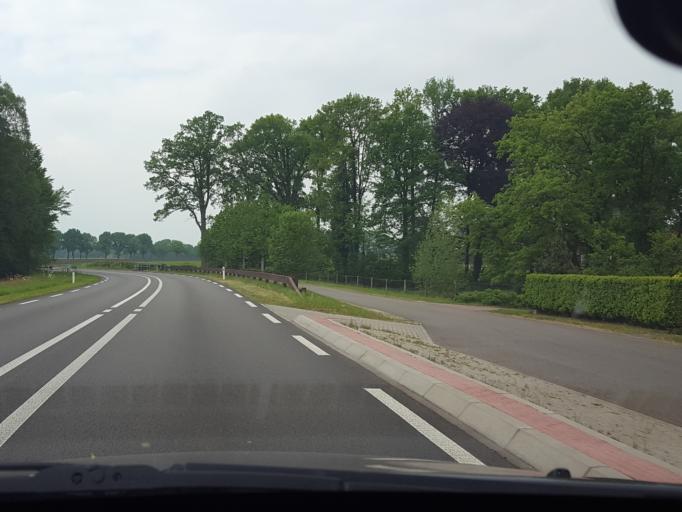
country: NL
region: Gelderland
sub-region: Gemeente Winterswijk
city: Winterswijk
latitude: 51.9455
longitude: 6.7717
